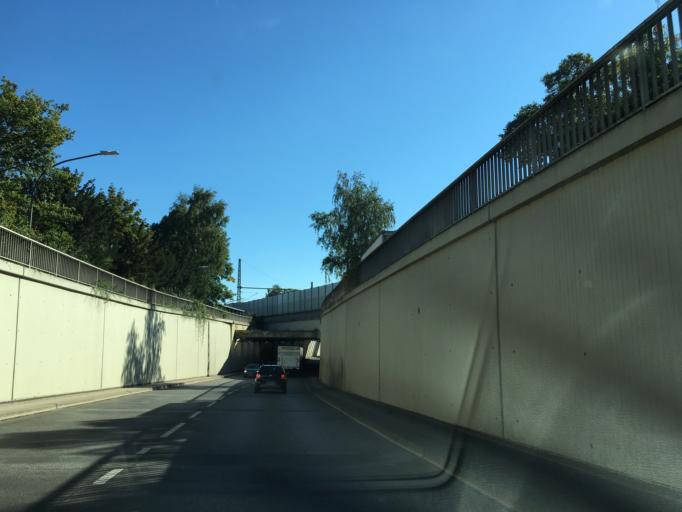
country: DE
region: Lower Saxony
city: Winsen
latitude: 53.3553
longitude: 10.2048
